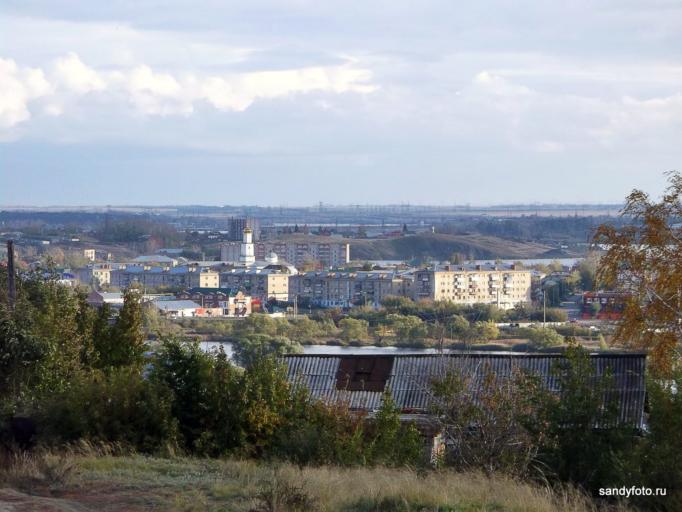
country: RU
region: Chelyabinsk
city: Troitsk
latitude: 54.0992
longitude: 61.5578
